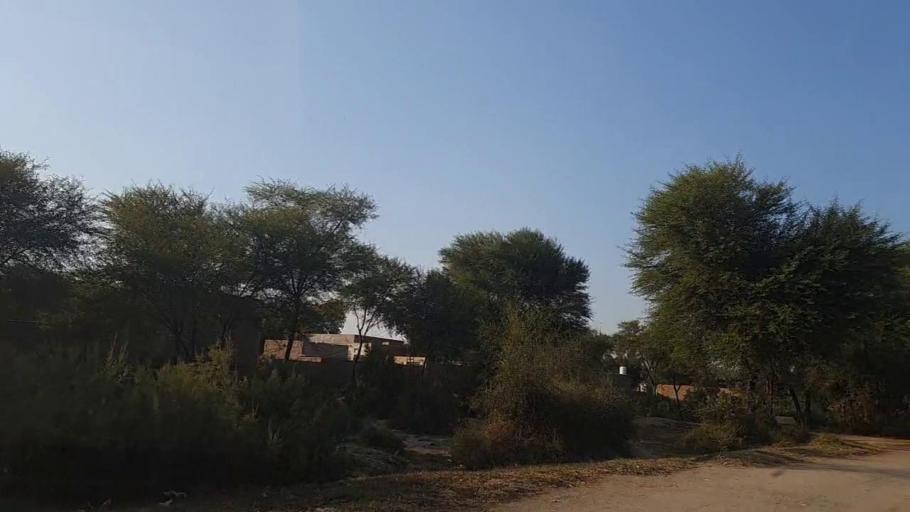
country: PK
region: Sindh
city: Sakrand
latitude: 26.3111
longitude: 68.1425
